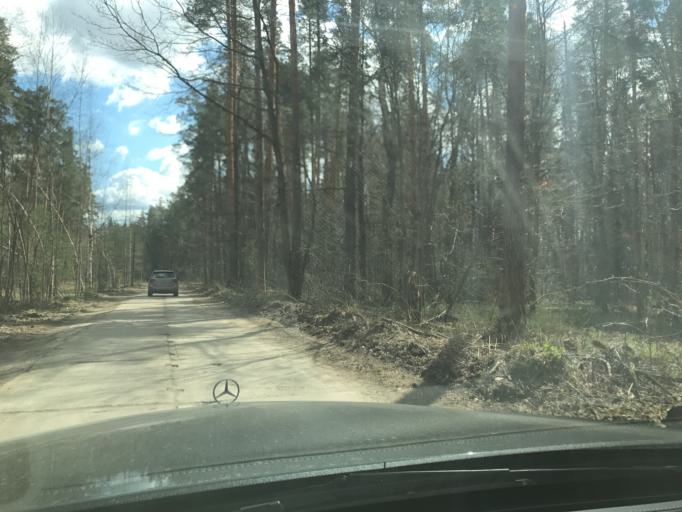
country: RU
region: Moskovskaya
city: Vereya
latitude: 55.8398
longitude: 39.1102
